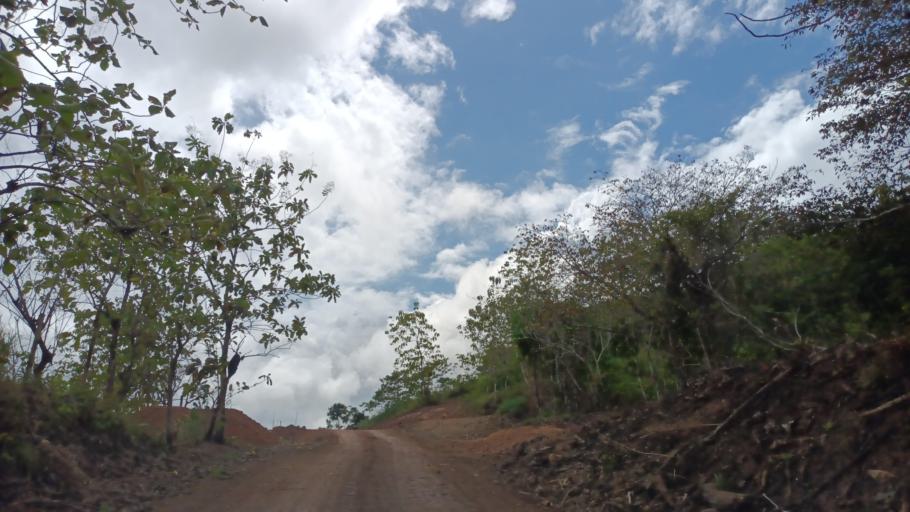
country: PA
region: Panama
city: La Cabima
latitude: 9.1162
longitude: -79.4977
